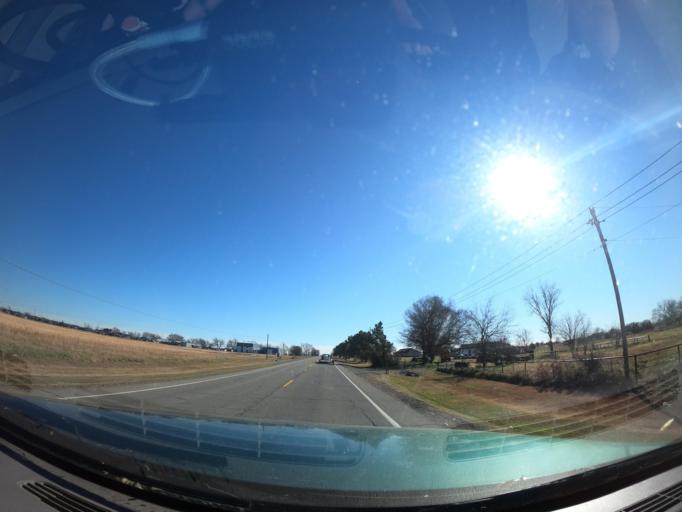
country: US
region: Oklahoma
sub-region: Muskogee County
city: Haskell
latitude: 35.8047
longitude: -95.6730
